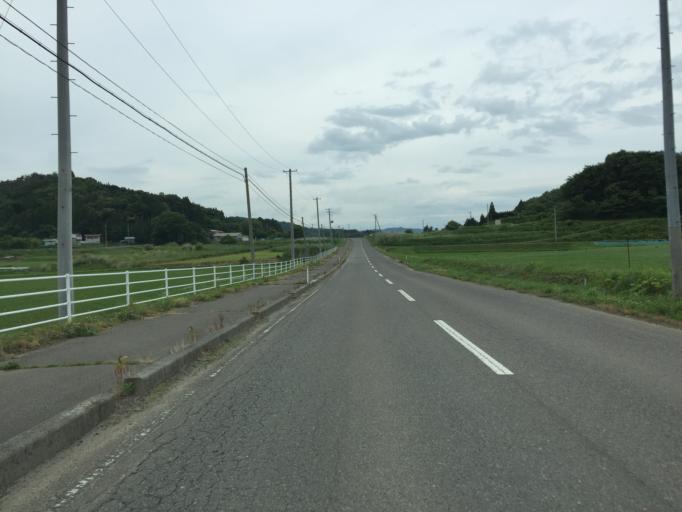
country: JP
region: Fukushima
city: Funehikimachi-funehiki
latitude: 37.3881
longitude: 140.5558
